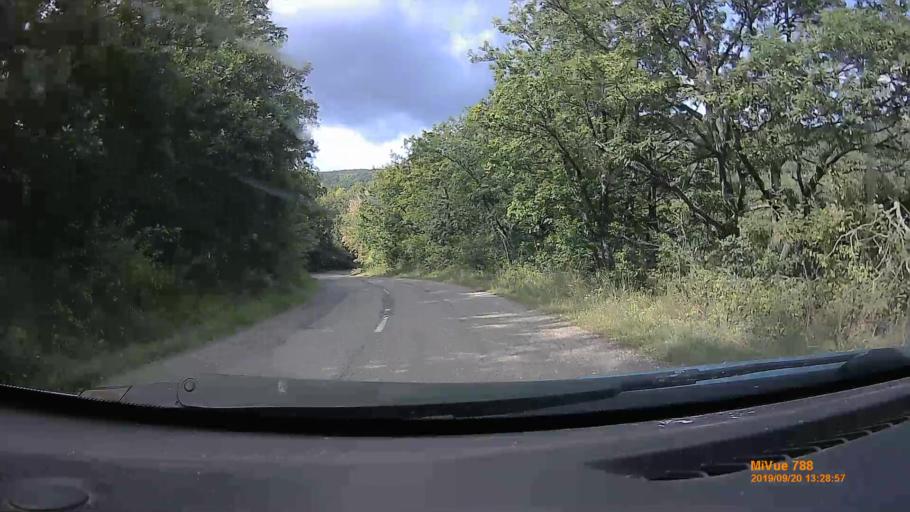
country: HU
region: Heves
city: Szilvasvarad
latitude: 48.0503
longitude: 20.4836
